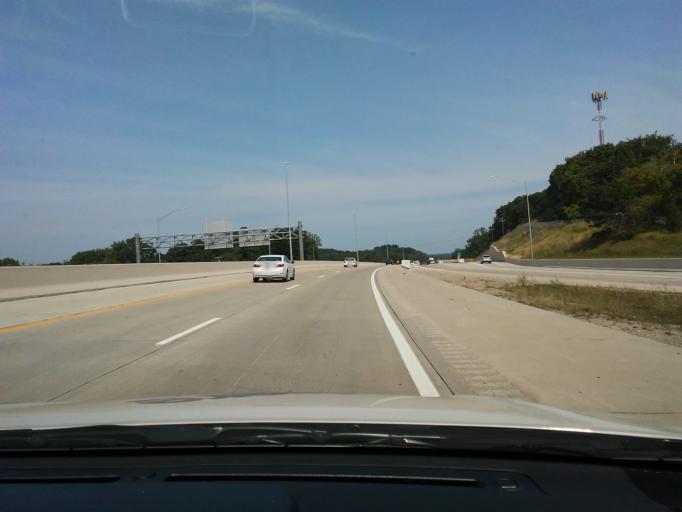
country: US
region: Michigan
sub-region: Livingston County
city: Brighton
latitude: 42.5269
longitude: -83.7617
